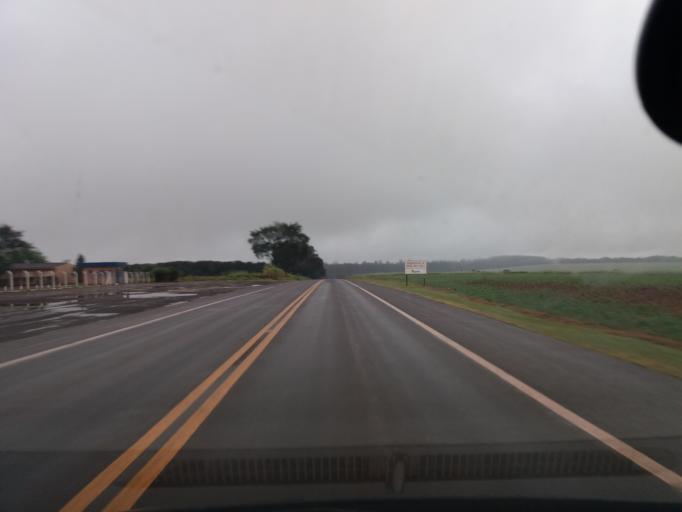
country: BR
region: Parana
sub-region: Campo Mourao
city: Campo Mourao
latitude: -24.2975
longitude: -52.5861
